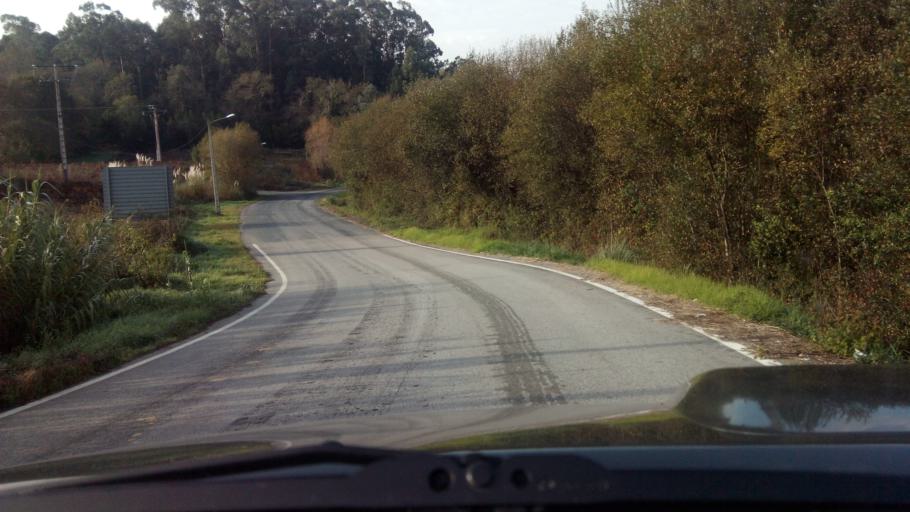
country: ES
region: Galicia
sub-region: Provincia de Pontevedra
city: Marin
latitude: 42.3665
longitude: -8.7205
